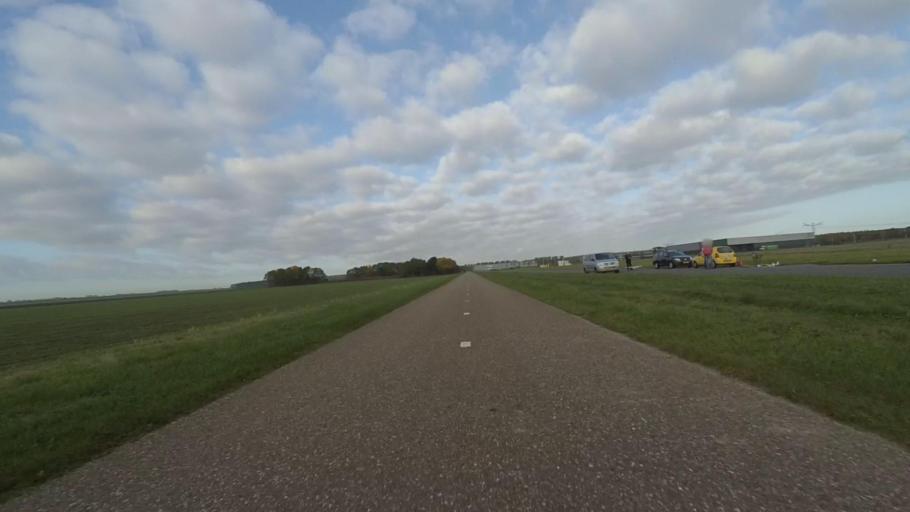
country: NL
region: Utrecht
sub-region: Gemeente Bunschoten
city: Spakenburg
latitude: 52.3130
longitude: 5.3234
